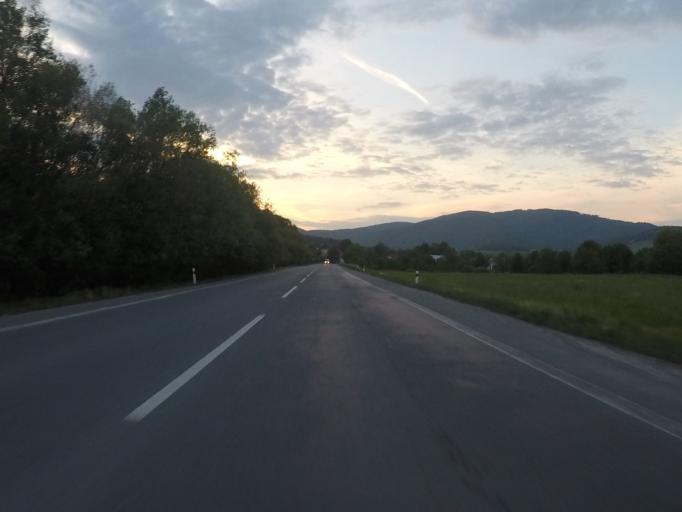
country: SK
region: Banskobystricky
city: Rimavska Sobota
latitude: 48.4966
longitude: 19.9384
